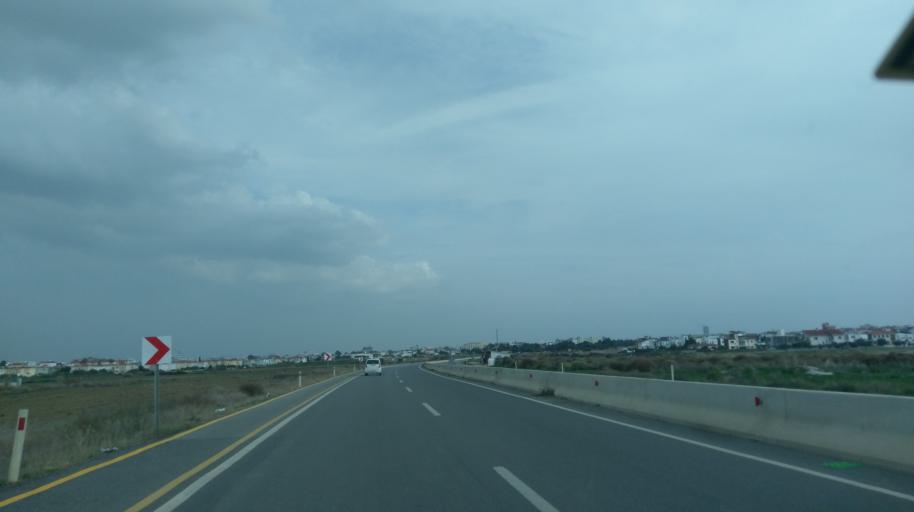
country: CY
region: Lefkosia
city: Nicosia
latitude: 35.1984
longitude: 33.3095
